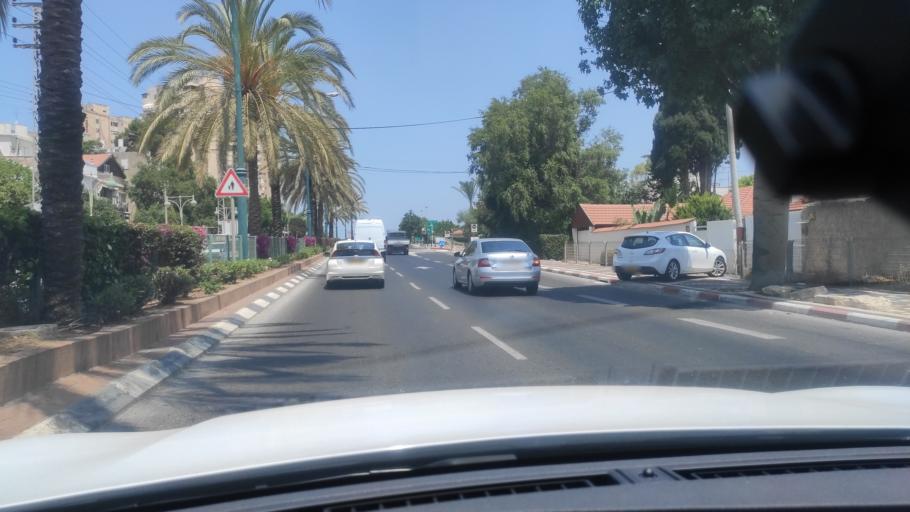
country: IL
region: Central District
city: Petah Tiqwa
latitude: 32.0984
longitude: 34.9005
